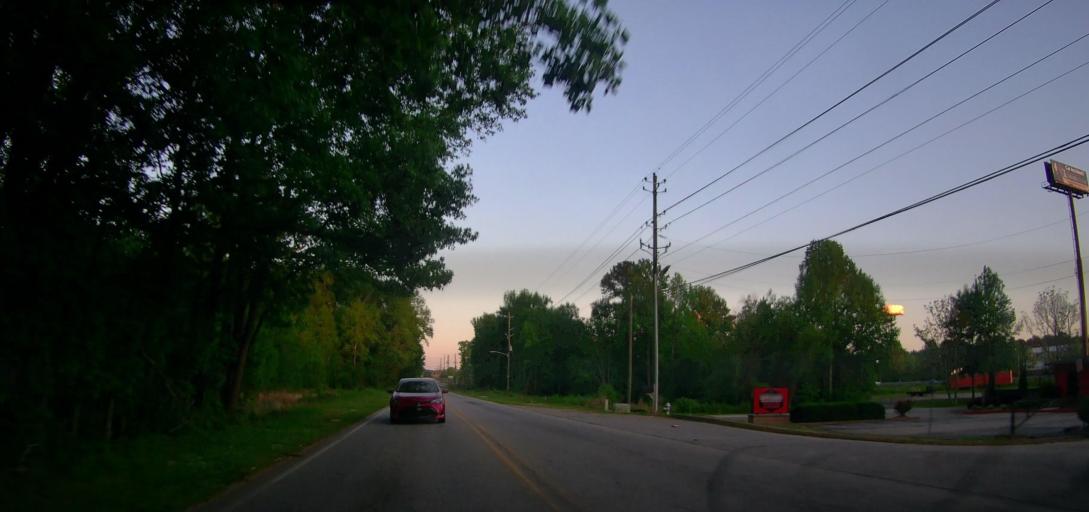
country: US
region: Georgia
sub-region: Henry County
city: McDonough
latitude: 33.4246
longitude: -84.1751
